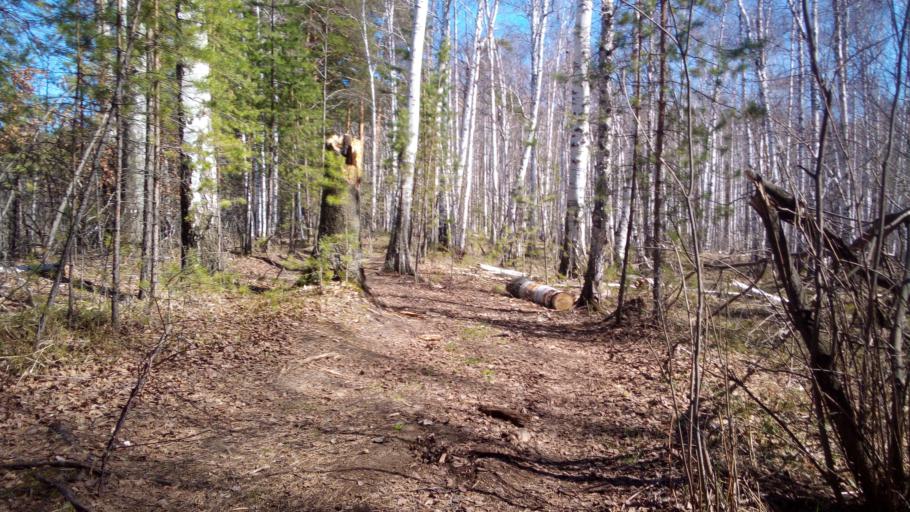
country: RU
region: Chelyabinsk
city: Chebarkul'
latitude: 55.1106
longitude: 60.3385
